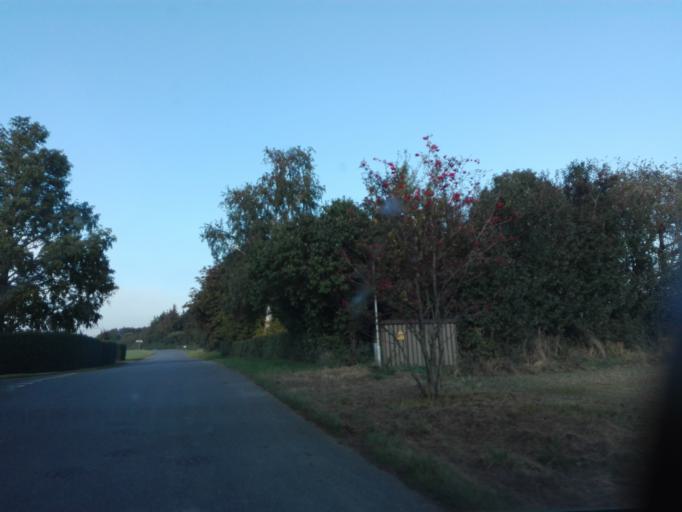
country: DK
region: Central Jutland
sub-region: Odder Kommune
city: Odder
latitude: 55.9462
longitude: 10.1949
